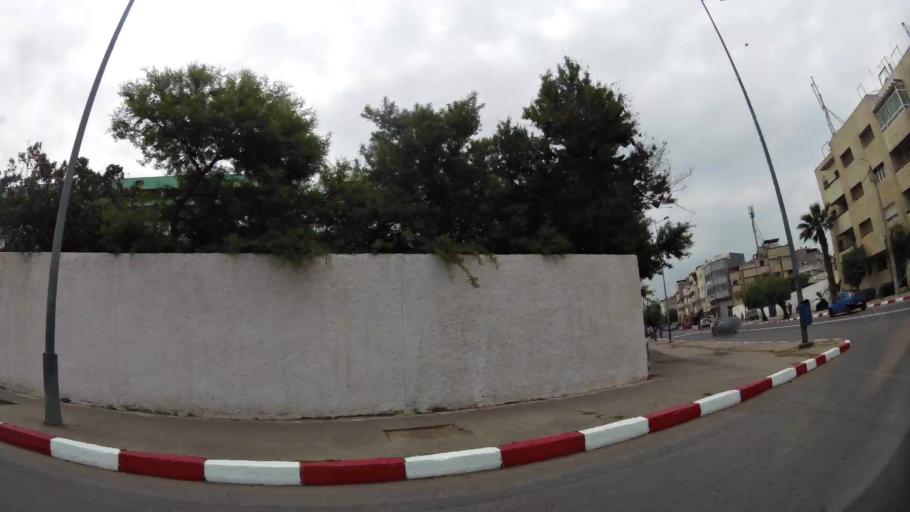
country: MA
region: Rabat-Sale-Zemmour-Zaer
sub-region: Rabat
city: Rabat
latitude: 33.9966
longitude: -6.8671
